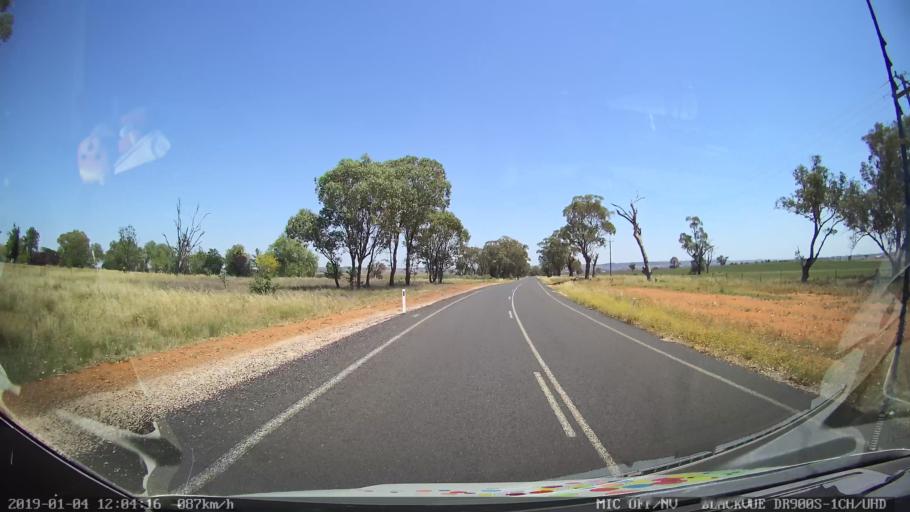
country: AU
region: New South Wales
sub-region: Wellington
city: Wellington
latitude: -32.7663
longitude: 148.6613
